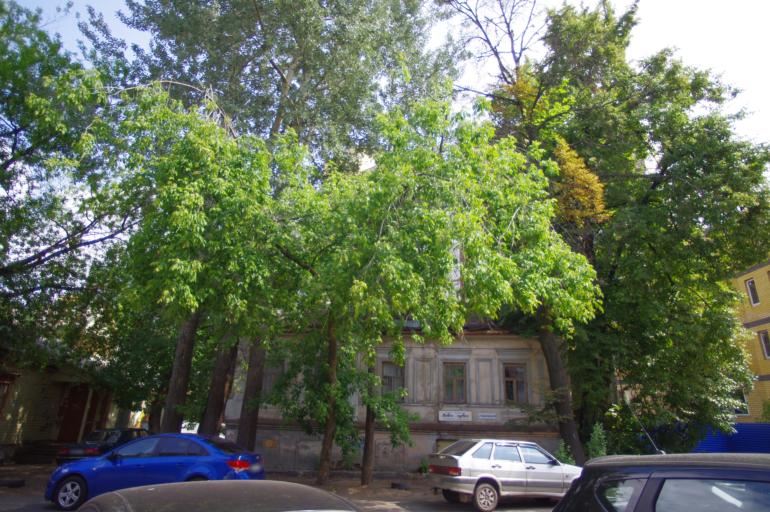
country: RU
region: Nizjnij Novgorod
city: Nizhniy Novgorod
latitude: 56.3100
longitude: 43.9935
